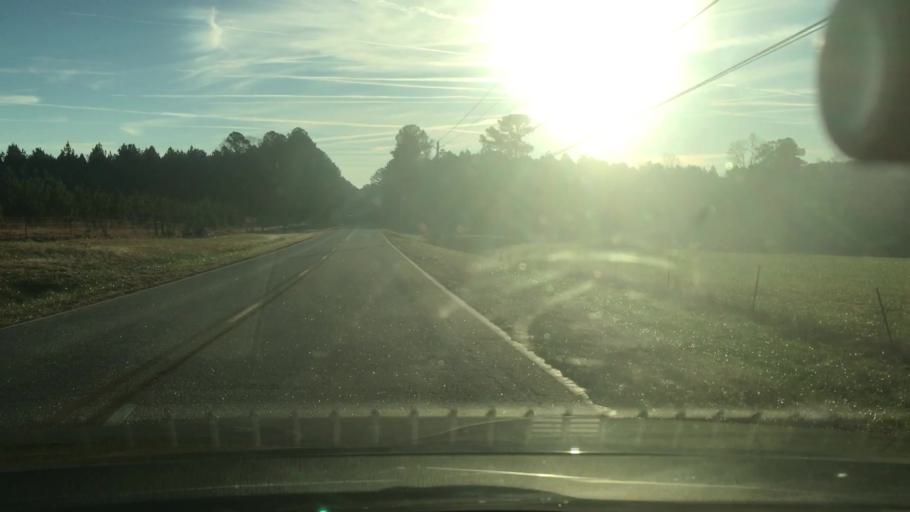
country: US
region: Georgia
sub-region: Spalding County
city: Experiment
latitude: 33.2630
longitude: -84.3036
